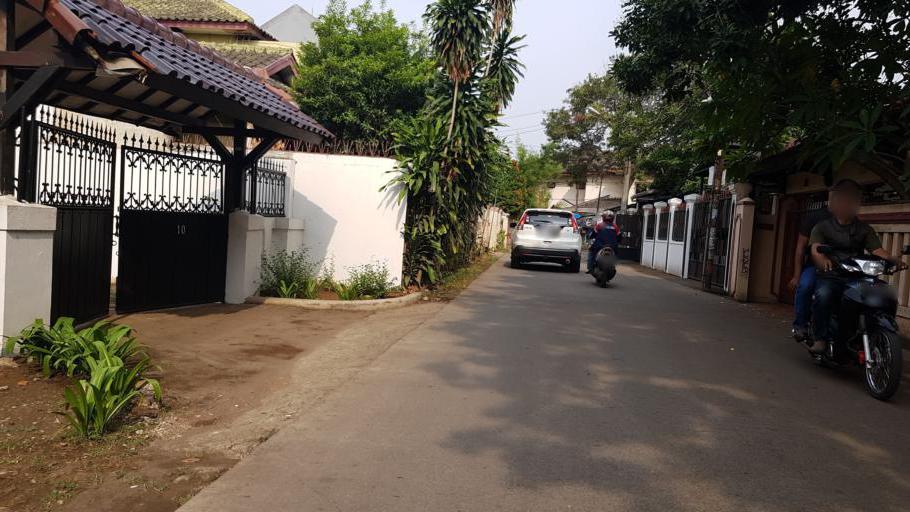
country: ID
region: West Java
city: Pamulang
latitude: -6.3256
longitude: 106.7977
